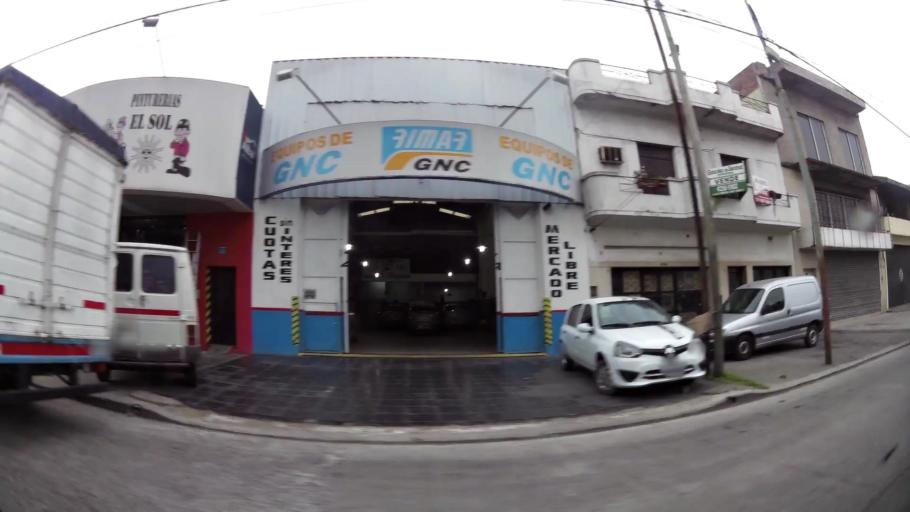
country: AR
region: Buenos Aires
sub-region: Partido de Lanus
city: Lanus
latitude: -34.6802
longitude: -58.4039
